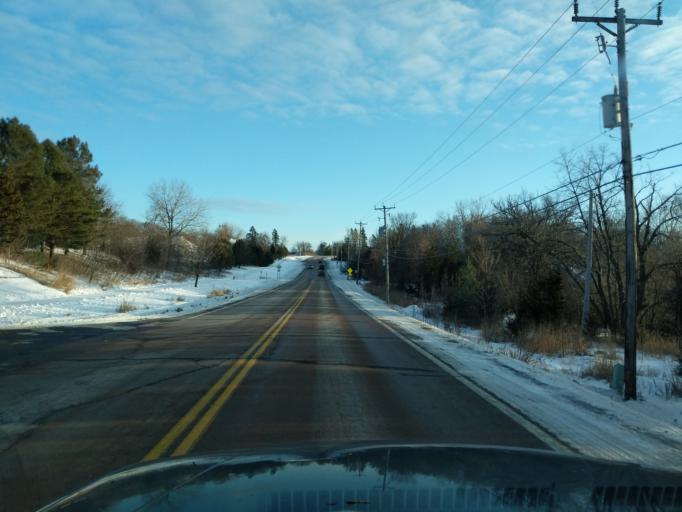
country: US
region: Minnesota
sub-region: Carver County
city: Victoria
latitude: 44.8732
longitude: -93.6402
